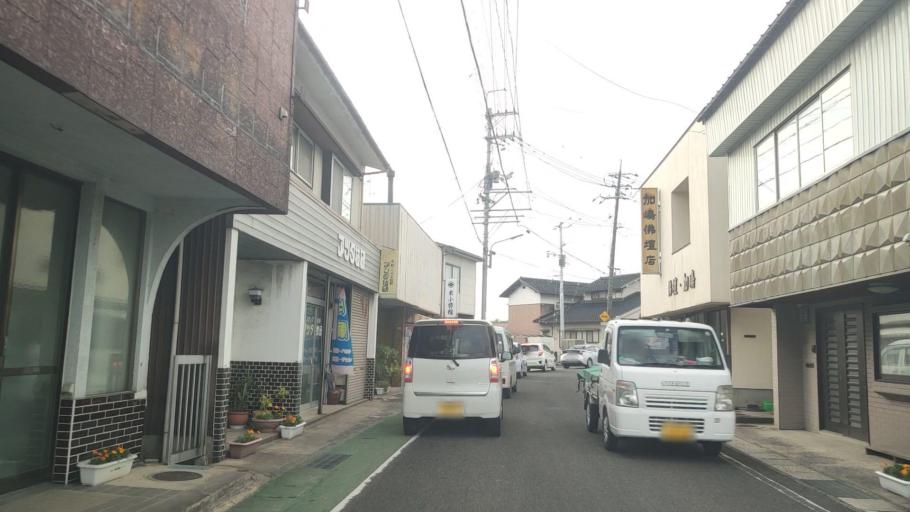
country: JP
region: Tottori
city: Kurayoshi
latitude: 35.4553
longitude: 133.8468
